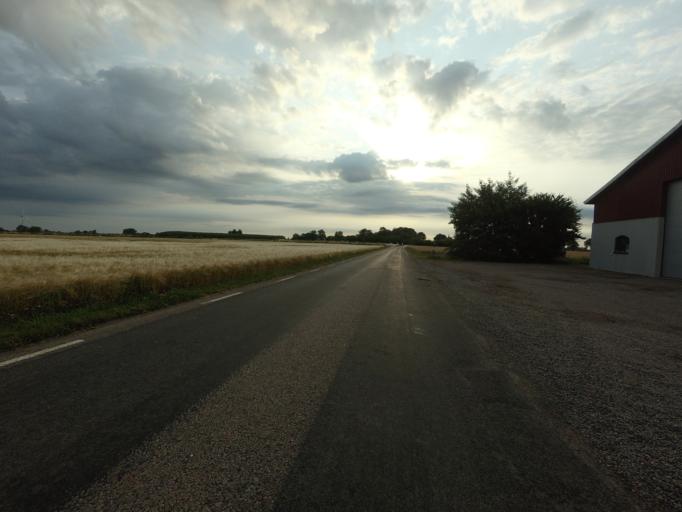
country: SE
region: Skane
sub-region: Hoganas Kommun
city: Hoganas
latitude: 56.1525
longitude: 12.6299
